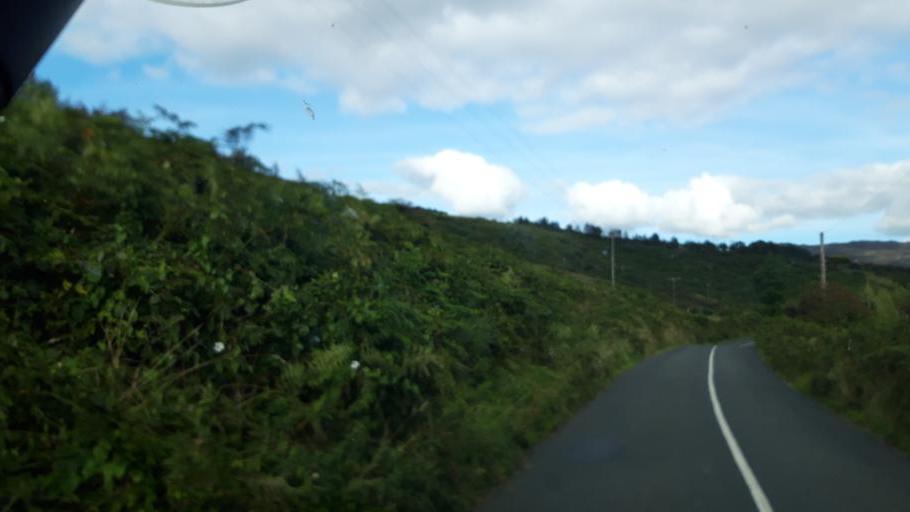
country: GB
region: Northern Ireland
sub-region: Down District
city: Warrenpoint
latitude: 54.0361
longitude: -6.2772
